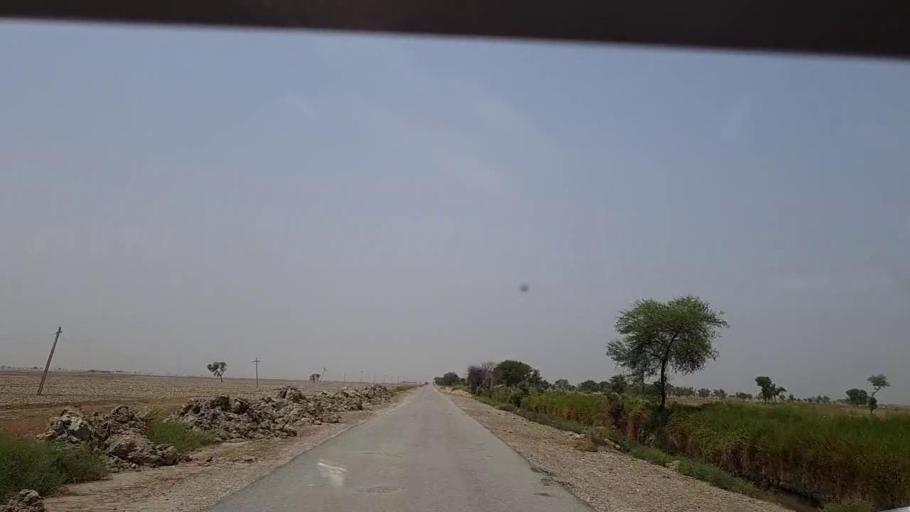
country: PK
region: Sindh
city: Khairpur Nathan Shah
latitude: 27.0235
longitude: 67.6211
